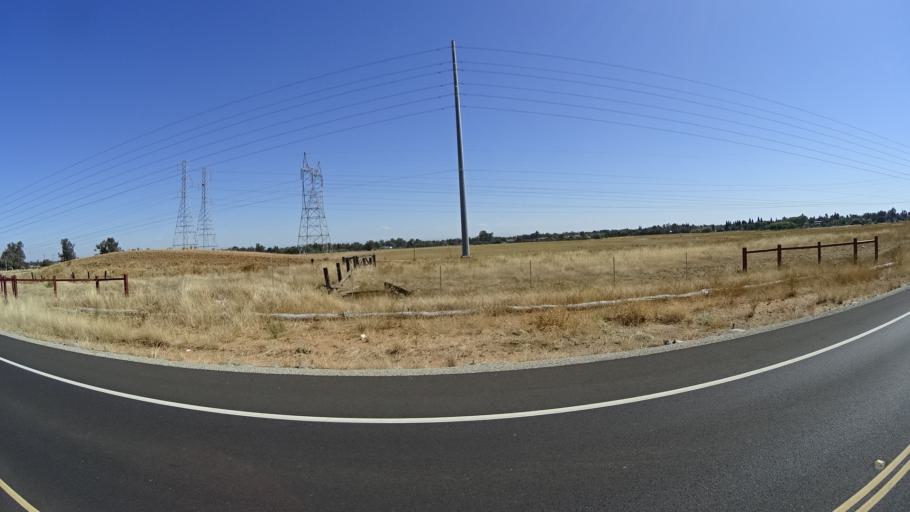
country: US
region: California
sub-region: Sacramento County
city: Vineyard
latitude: 38.4353
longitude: -121.3533
